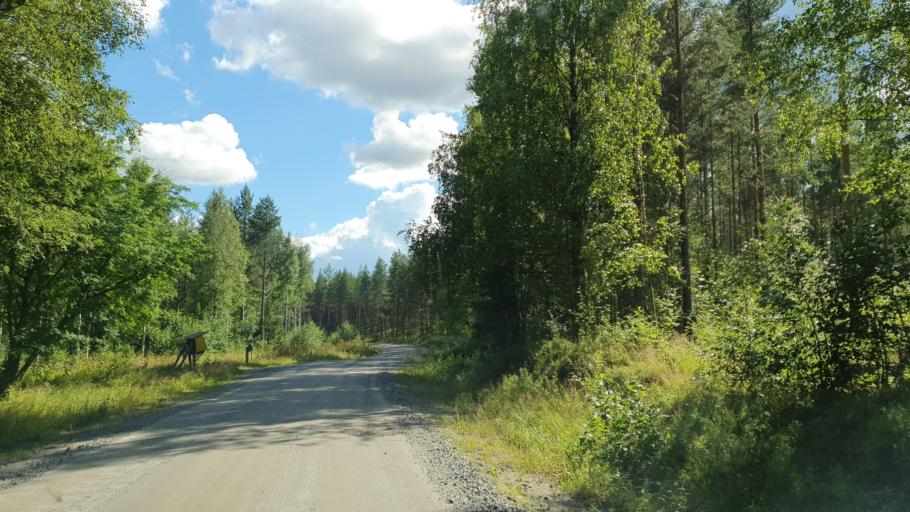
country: FI
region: Kainuu
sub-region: Kehys-Kainuu
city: Kuhmo
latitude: 64.1012
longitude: 29.4032
